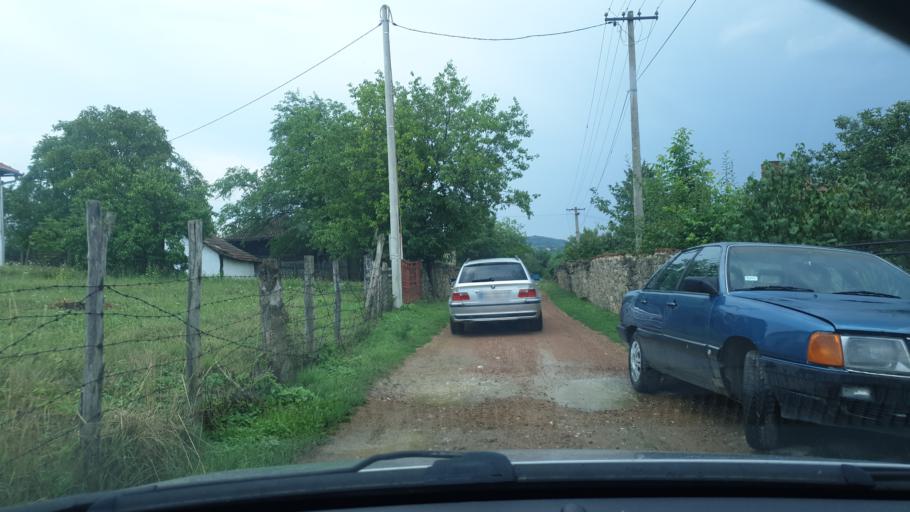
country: RS
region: Central Serbia
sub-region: Sumadijski Okrug
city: Kragujevac
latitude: 44.0787
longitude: 20.7984
